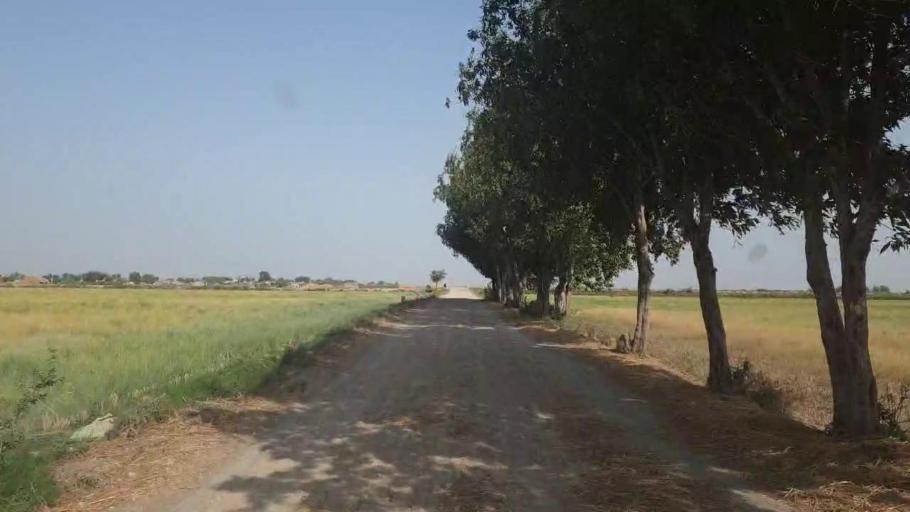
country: PK
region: Sindh
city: Kario
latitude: 24.5357
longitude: 68.5426
